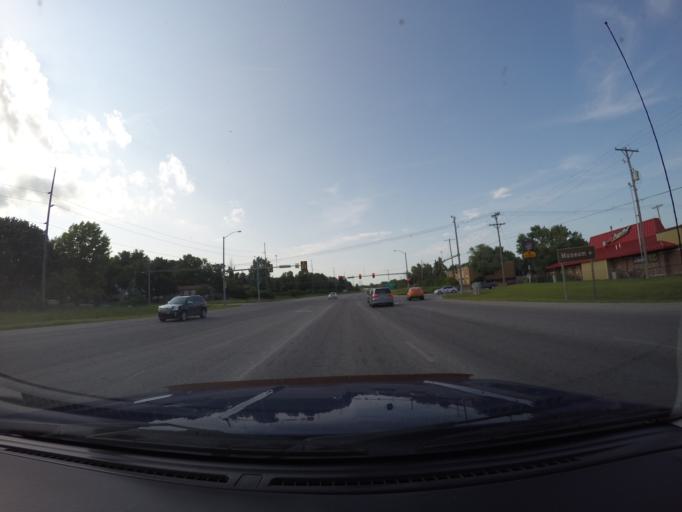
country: US
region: Kansas
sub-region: Riley County
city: Manhattan
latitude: 39.1923
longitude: -96.6123
